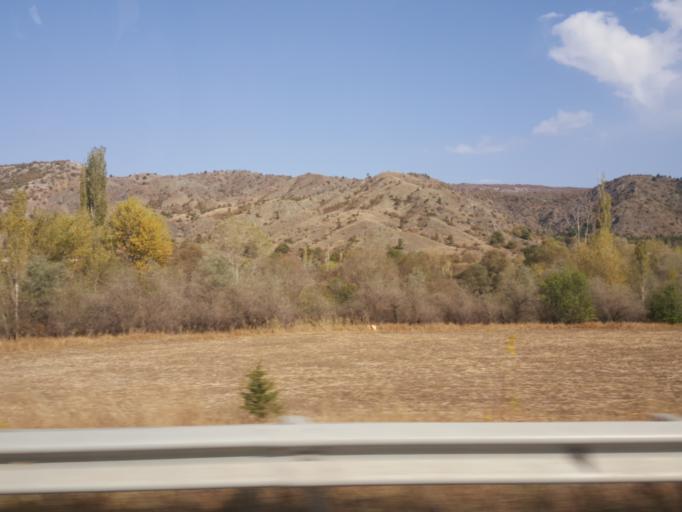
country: TR
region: Corum
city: Seydim
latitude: 40.3691
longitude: 34.7294
